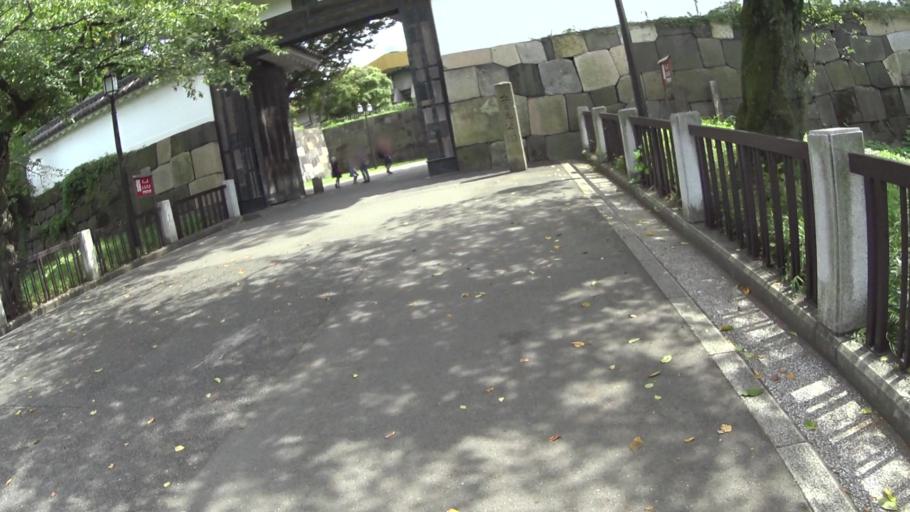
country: JP
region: Tokyo
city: Tokyo
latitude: 35.6944
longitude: 139.7493
